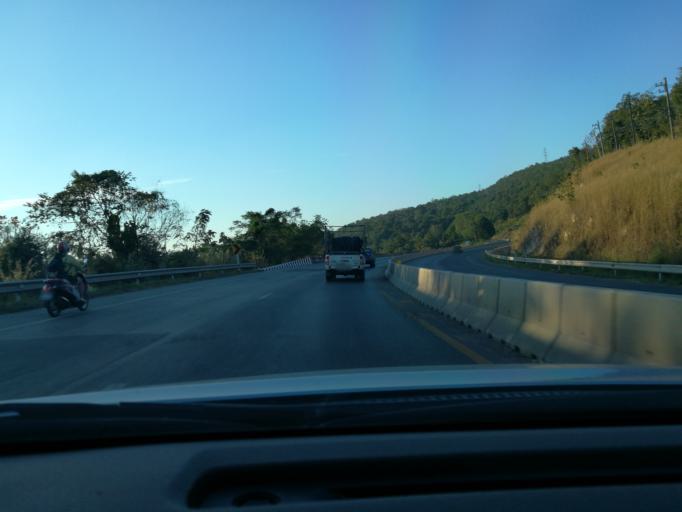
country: TH
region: Phitsanulok
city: Wang Thong
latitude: 16.8503
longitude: 100.5168
